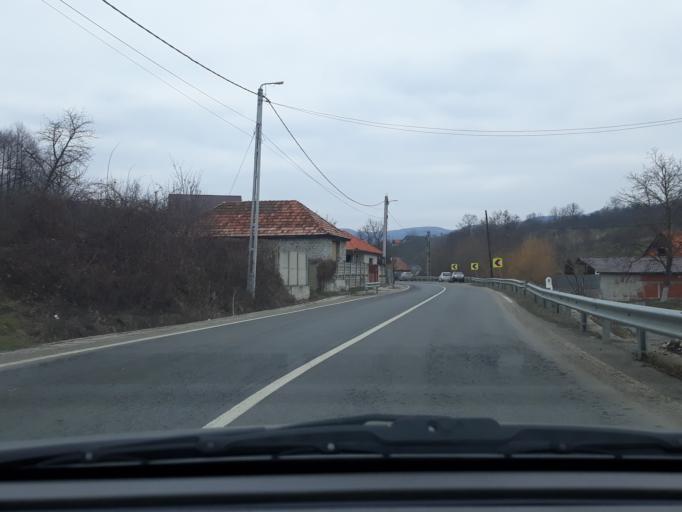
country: RO
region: Bihor
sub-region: Oras Alesd
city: Pestis
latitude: 47.0750
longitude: 22.4129
